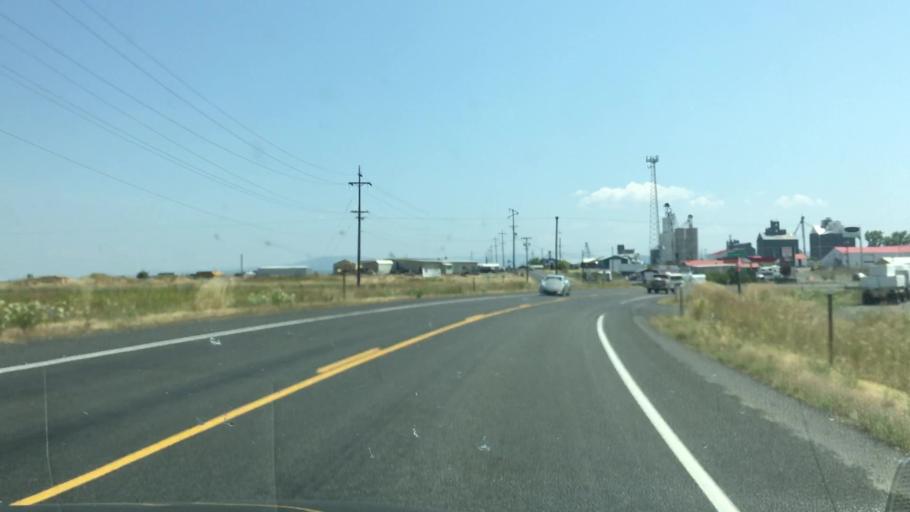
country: US
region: Idaho
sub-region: Idaho County
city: Grangeville
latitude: 45.9360
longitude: -116.1364
